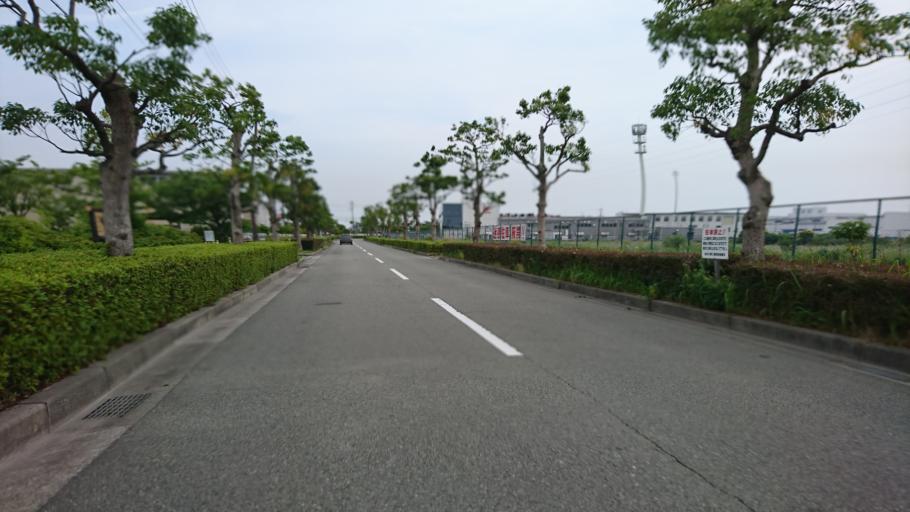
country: JP
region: Hyogo
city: Kakogawacho-honmachi
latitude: 34.7398
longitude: 134.8841
